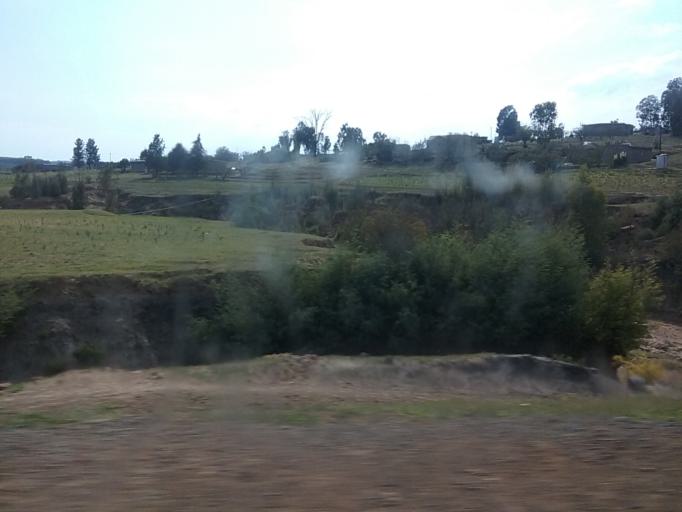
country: LS
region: Berea
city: Teyateyaneng
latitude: -29.0895
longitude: 27.9296
